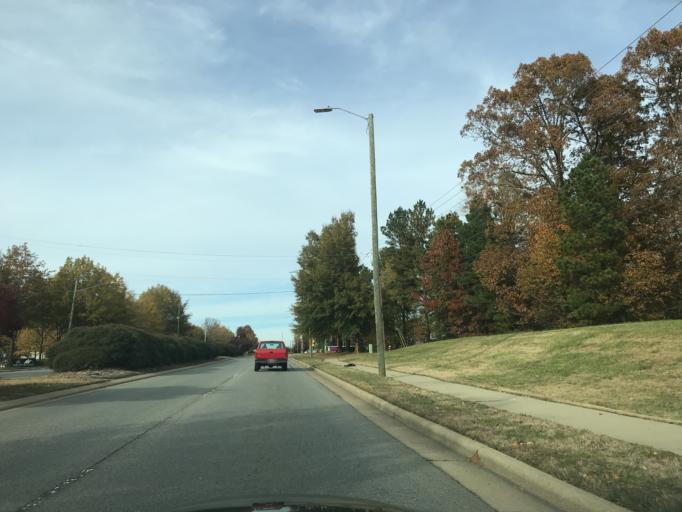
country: US
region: North Carolina
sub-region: Wake County
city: West Raleigh
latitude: 35.8961
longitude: -78.6804
